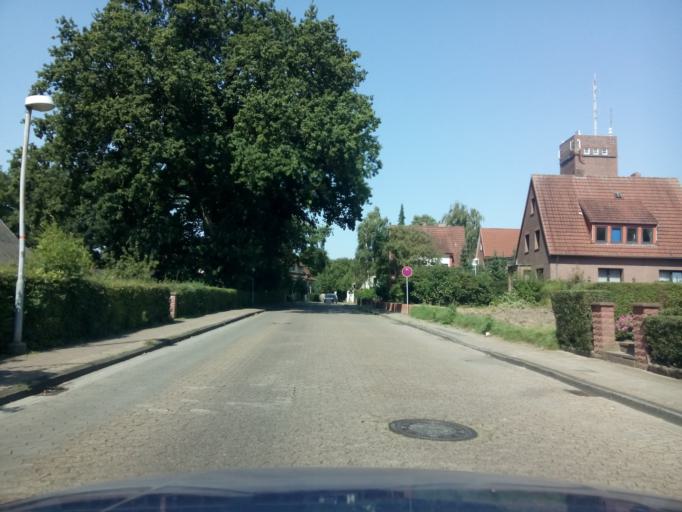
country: DE
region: Lower Saxony
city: Osterholz-Scharmbeck
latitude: 53.2307
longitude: 8.7889
